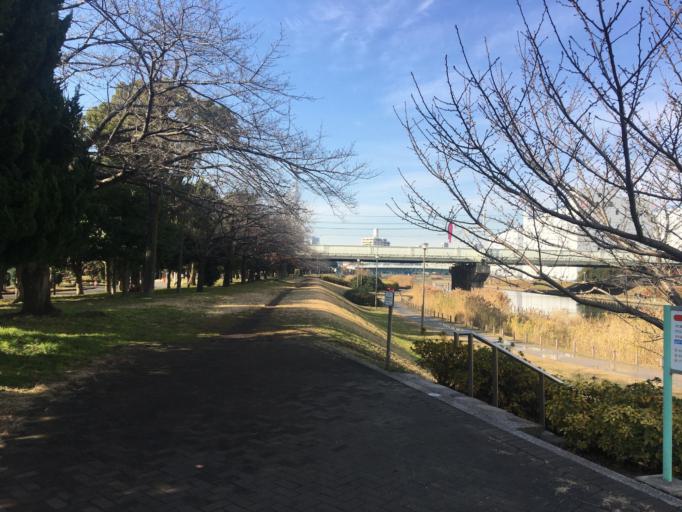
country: JP
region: Tokyo
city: Urayasu
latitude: 35.7010
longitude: 139.8394
